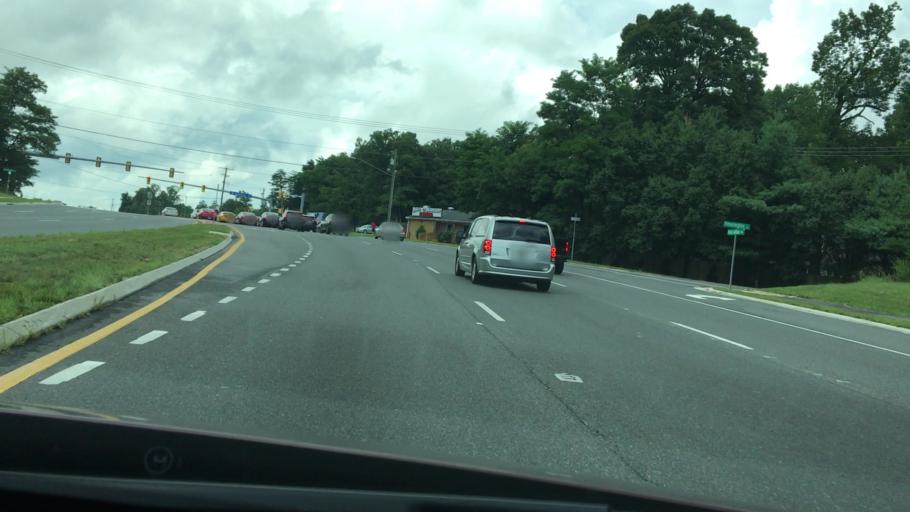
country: US
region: Virginia
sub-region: Prince William County
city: Dale City
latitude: 38.6631
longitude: -77.3272
